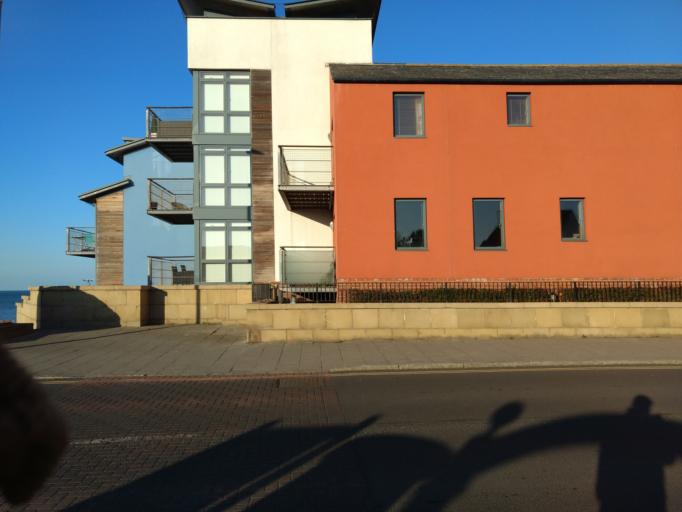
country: GB
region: England
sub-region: Northumberland
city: North Sunderland
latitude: 55.5825
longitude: -1.6542
